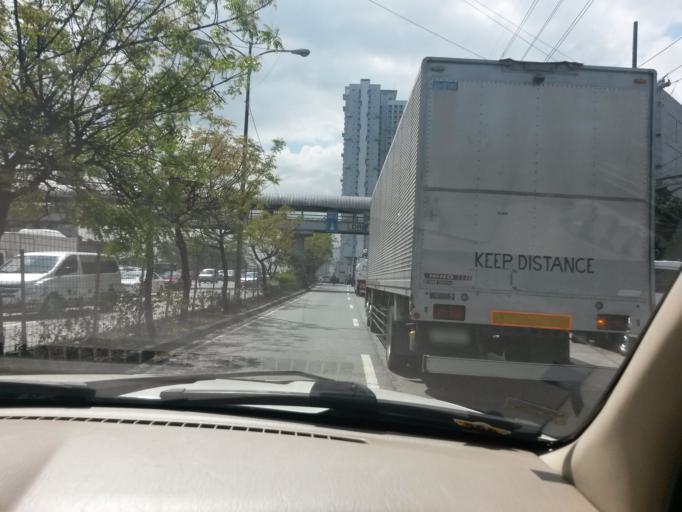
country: PH
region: Metro Manila
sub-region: Quezon City
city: Quezon City
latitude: 14.6475
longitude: 121.0744
